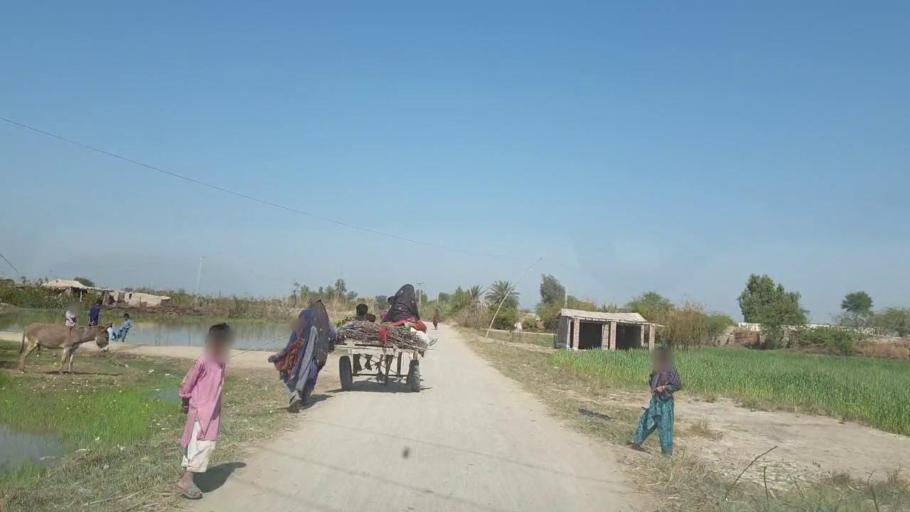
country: PK
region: Sindh
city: Mirpur Khas
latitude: 25.7225
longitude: 69.1172
